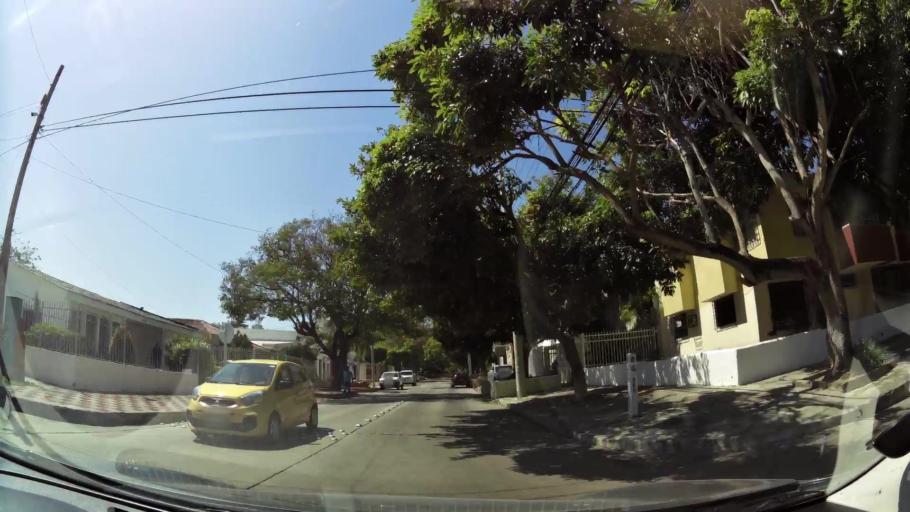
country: CO
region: Atlantico
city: Barranquilla
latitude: 11.0055
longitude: -74.7958
